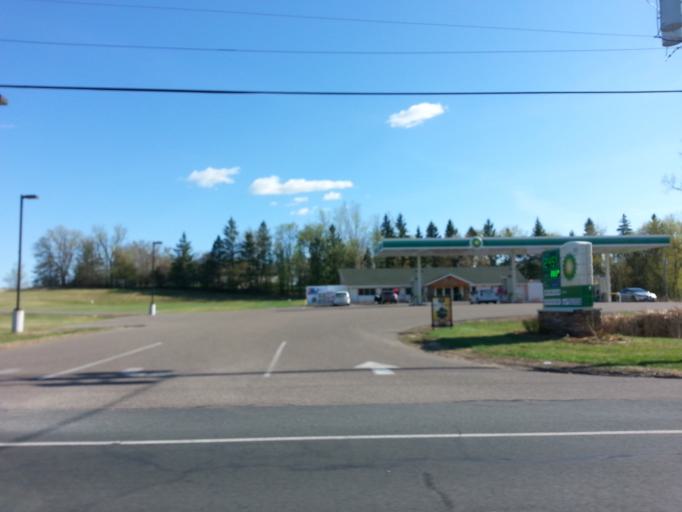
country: US
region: Wisconsin
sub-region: Saint Croix County
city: North Hudson
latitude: 45.0216
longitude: -92.6663
